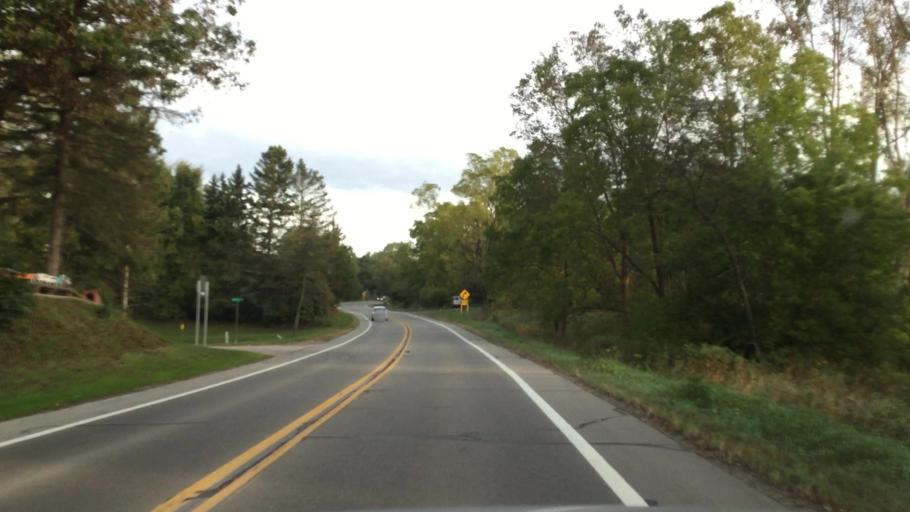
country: US
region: Michigan
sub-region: Livingston County
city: Whitmore Lake
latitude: 42.4466
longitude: -83.7833
